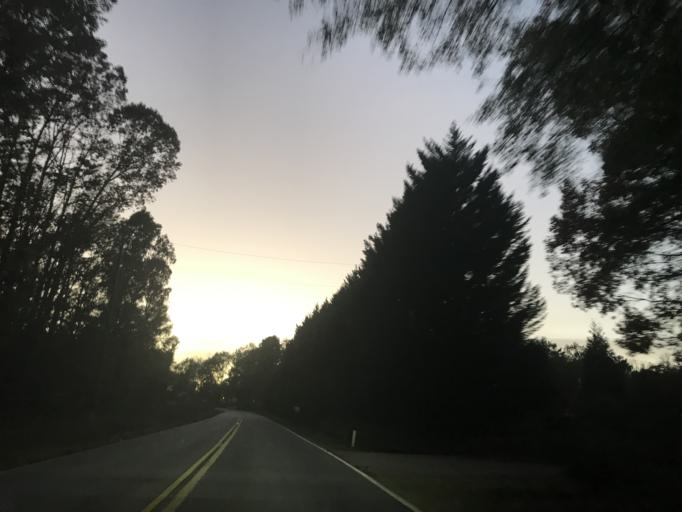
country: US
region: South Carolina
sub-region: Spartanburg County
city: Mayo
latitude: 35.0873
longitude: -81.8949
